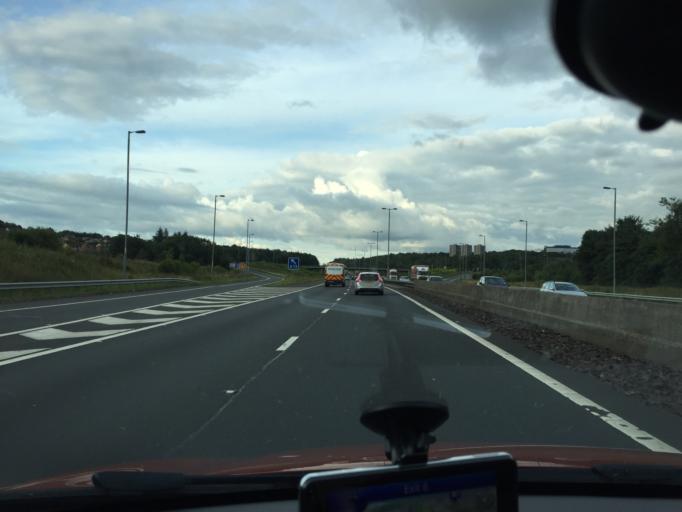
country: GB
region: Scotland
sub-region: North Lanarkshire
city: Cumbernauld
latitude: 55.9413
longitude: -4.0182
